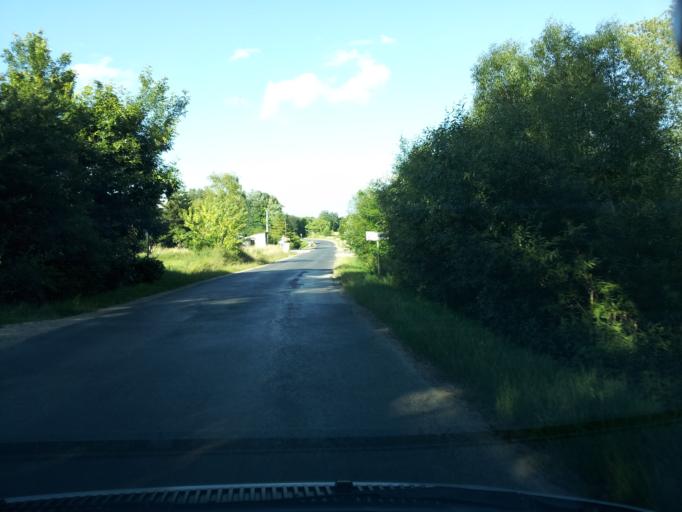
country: HU
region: Veszprem
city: Zirc
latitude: 47.2292
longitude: 17.8331
